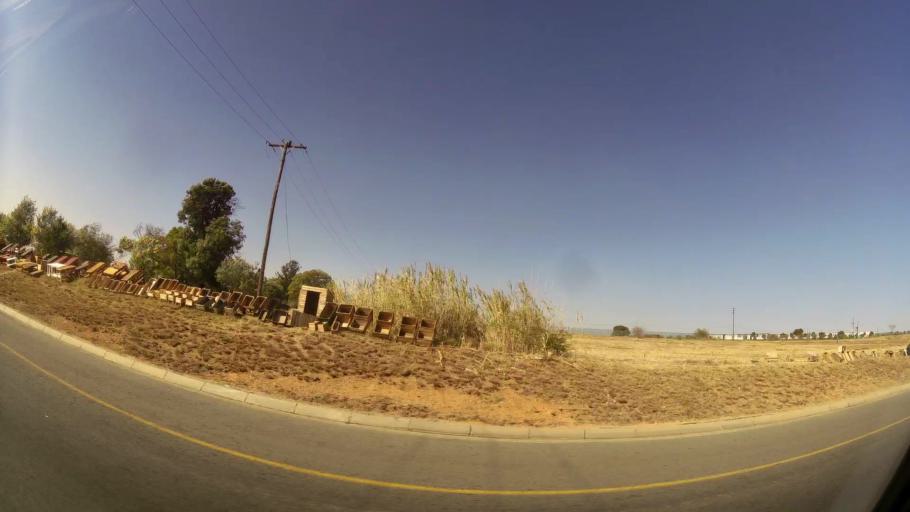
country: ZA
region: Gauteng
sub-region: West Rand District Municipality
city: Muldersdriseloop
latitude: -25.9911
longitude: 27.9247
